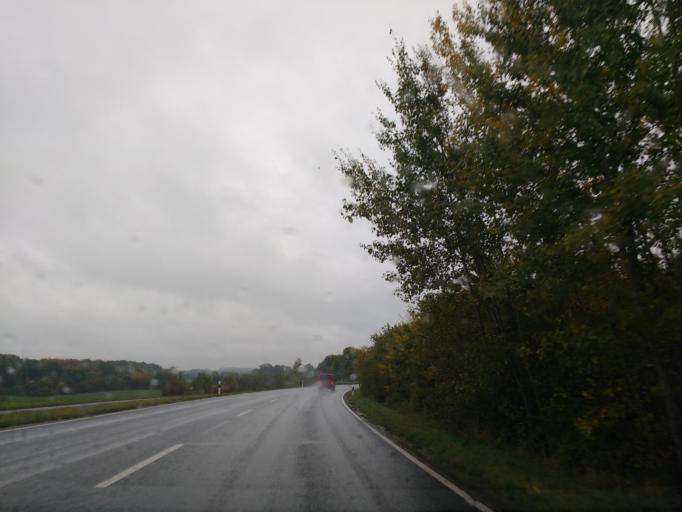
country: DE
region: Schleswig-Holstein
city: Eutin
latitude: 54.1162
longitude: 10.6537
